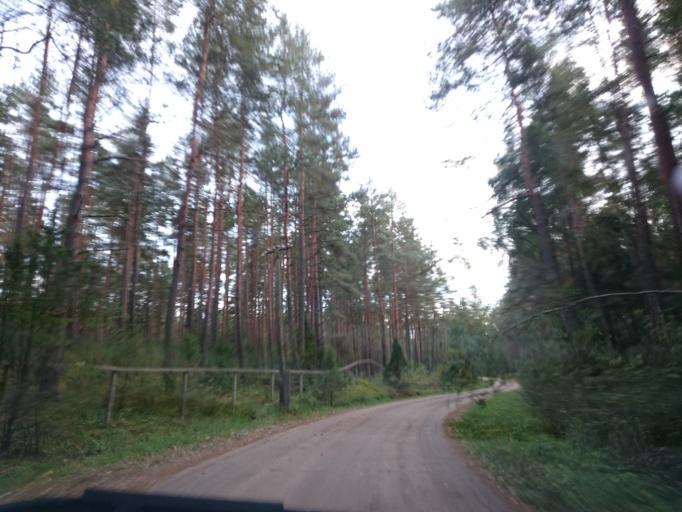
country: LV
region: Garkalne
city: Garkalne
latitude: 57.0470
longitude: 24.3839
